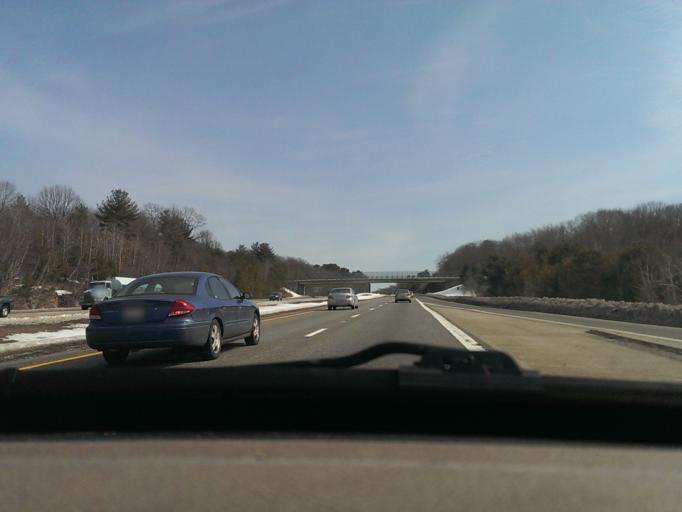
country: US
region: Massachusetts
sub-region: Worcester County
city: Millville
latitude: 42.0206
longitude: -71.5993
